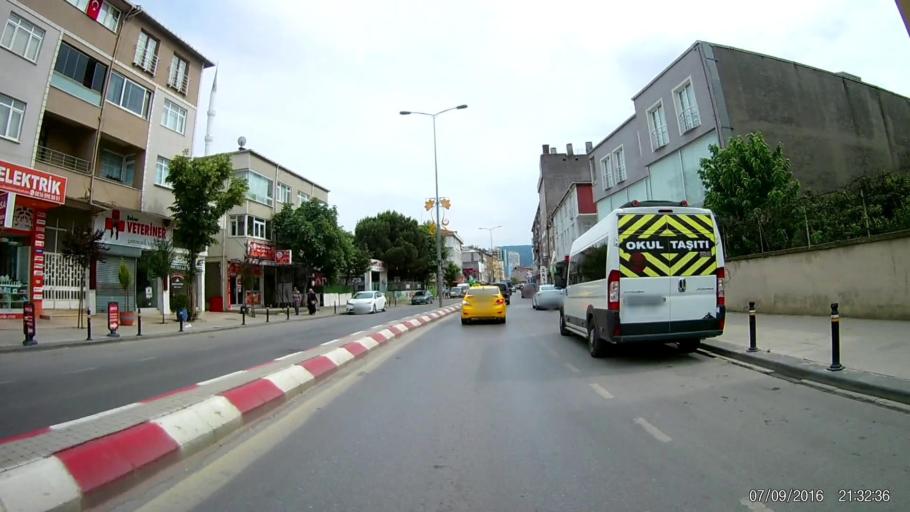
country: TR
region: Istanbul
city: Sultanbeyli
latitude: 40.9793
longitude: 29.2657
